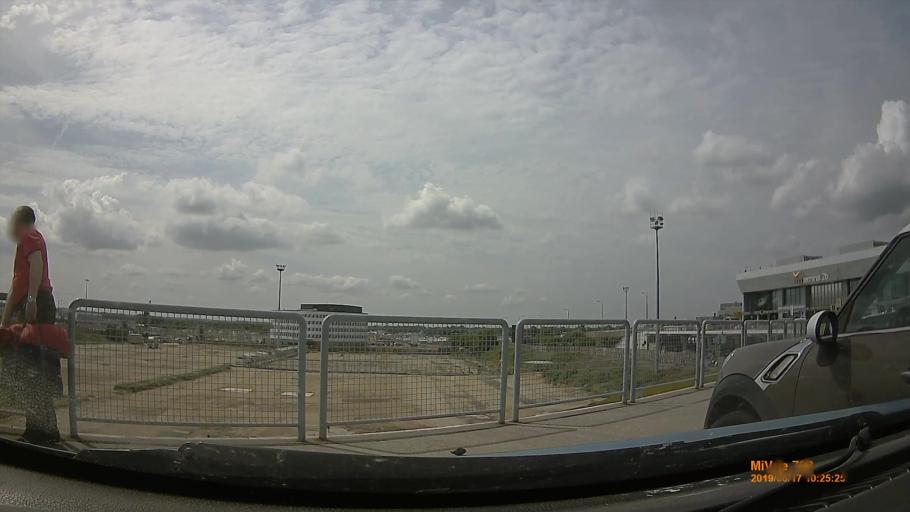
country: HU
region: Pest
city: Vecses
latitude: 47.4329
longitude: 19.2618
